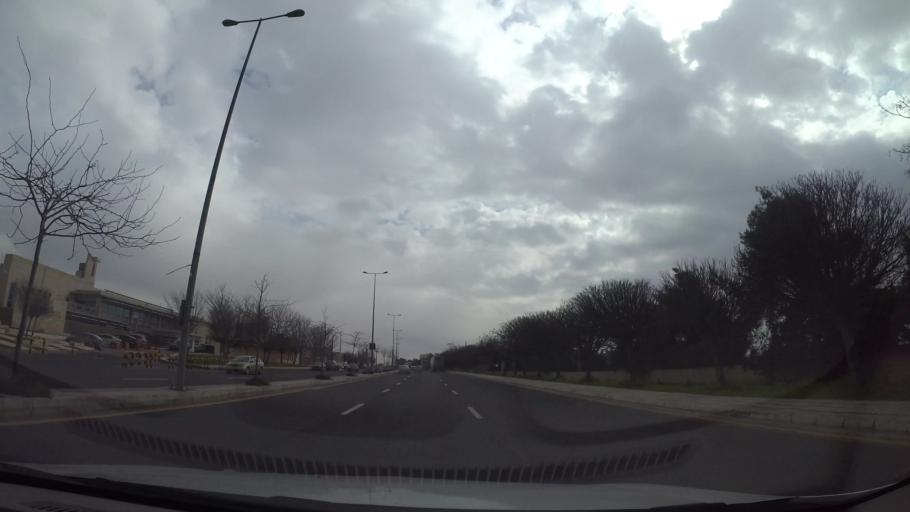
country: JO
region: Amman
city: Wadi as Sir
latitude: 31.9800
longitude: 35.8248
